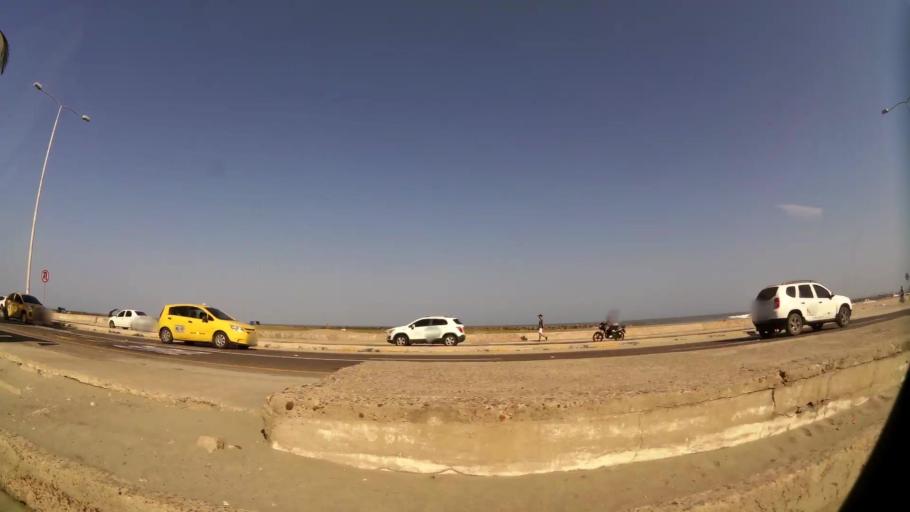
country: CO
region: Bolivar
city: Cartagena
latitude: 10.4343
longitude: -75.5399
